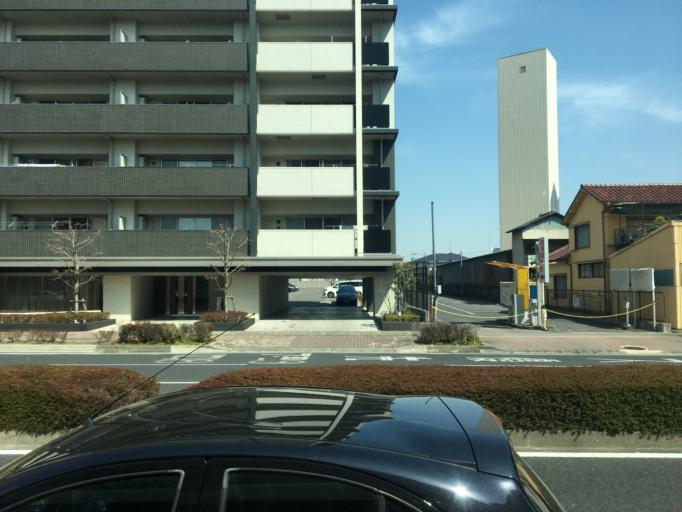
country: JP
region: Tochigi
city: Utsunomiya-shi
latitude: 36.5631
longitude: 139.8709
